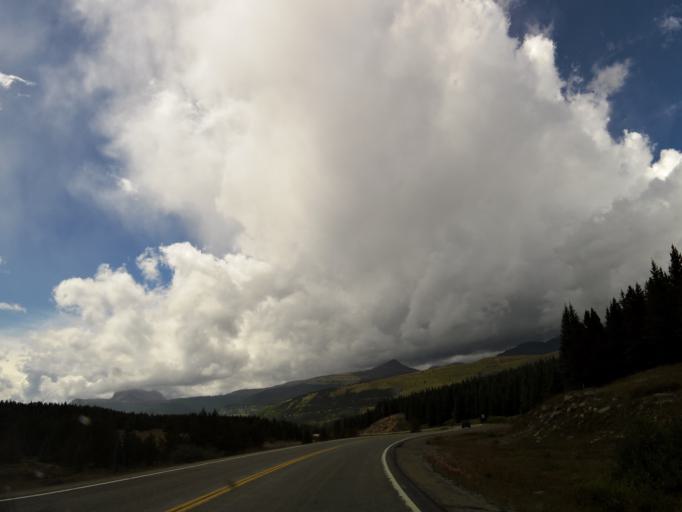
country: US
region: Colorado
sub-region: San Juan County
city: Silverton
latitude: 37.7338
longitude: -107.7044
